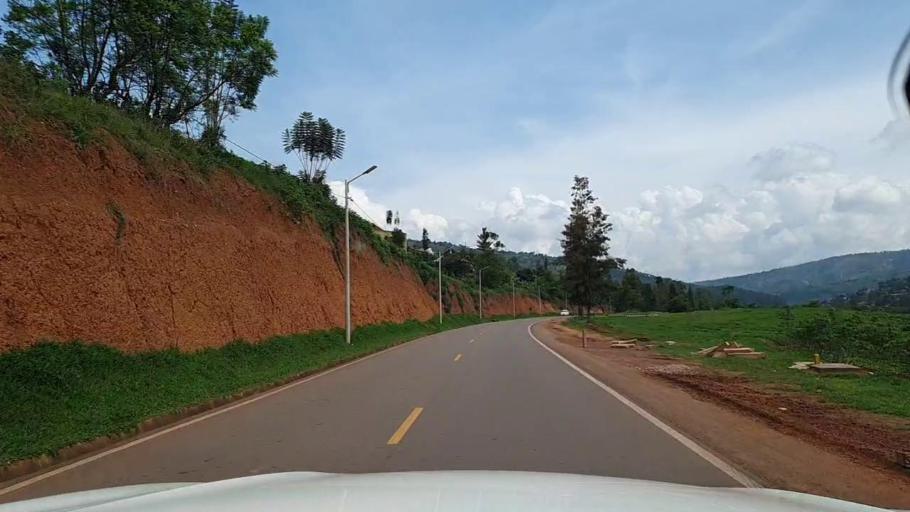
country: RW
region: Kigali
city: Kigali
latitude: -1.8735
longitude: 30.0825
